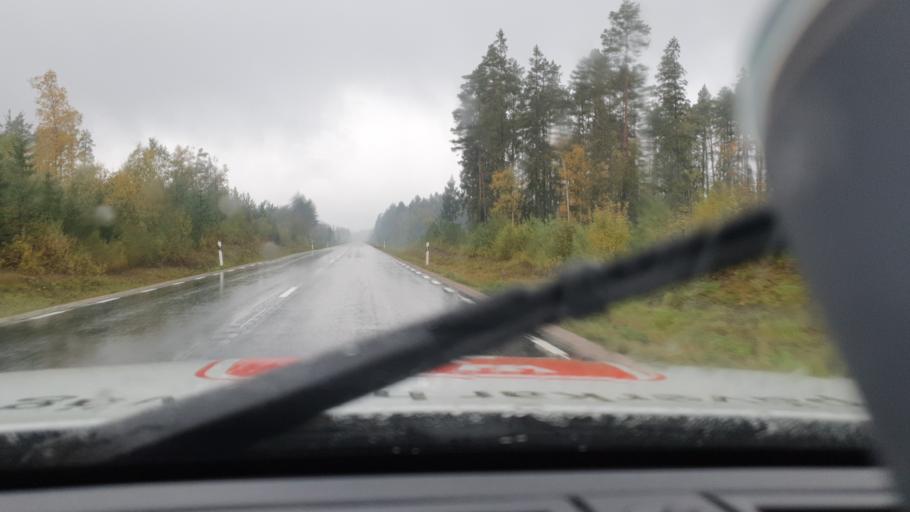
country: SE
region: Uppsala
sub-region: Tierps Kommun
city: Tierp
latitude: 60.3046
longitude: 17.5610
